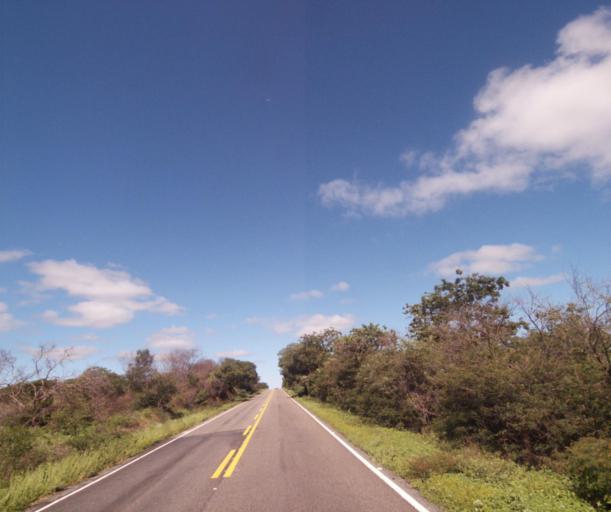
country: BR
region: Bahia
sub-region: Palmas De Monte Alto
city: Palmas de Monte Alto
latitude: -14.2388
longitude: -43.0280
